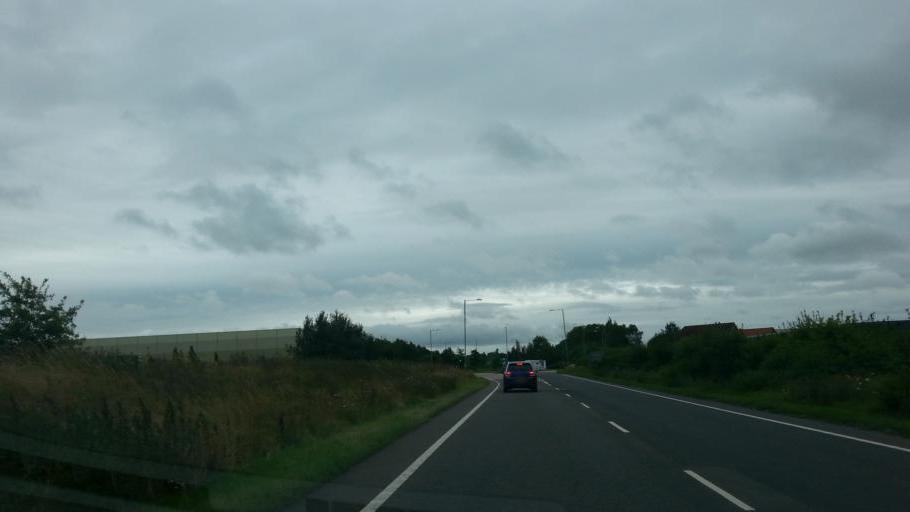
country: GB
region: England
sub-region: Wiltshire
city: Melksham
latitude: 51.3564
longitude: -2.1380
